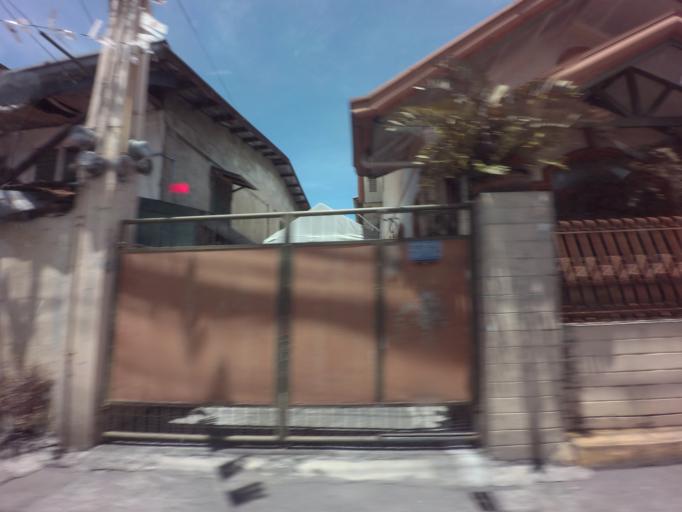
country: PH
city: Sambayanihan People's Village
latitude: 14.4937
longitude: 120.9901
